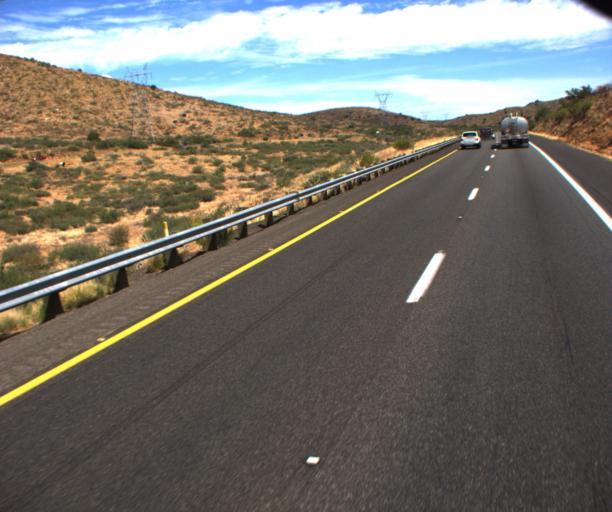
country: US
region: Arizona
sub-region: Yavapai County
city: Cordes Lakes
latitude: 34.2955
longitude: -112.1248
